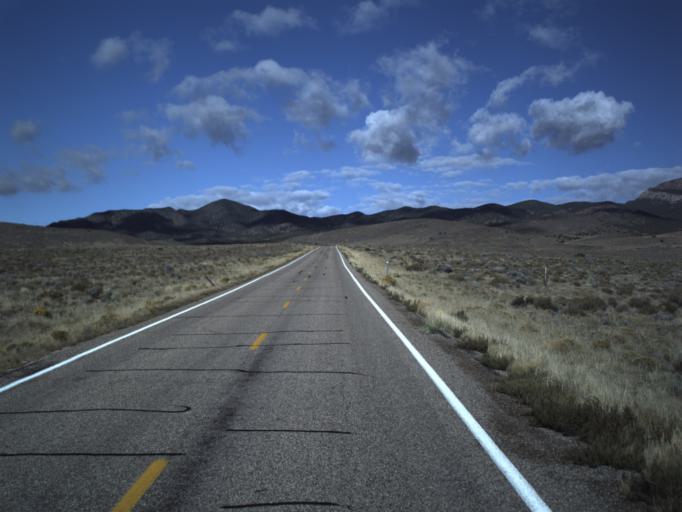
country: US
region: Utah
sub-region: Beaver County
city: Milford
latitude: 38.4549
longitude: -113.2133
